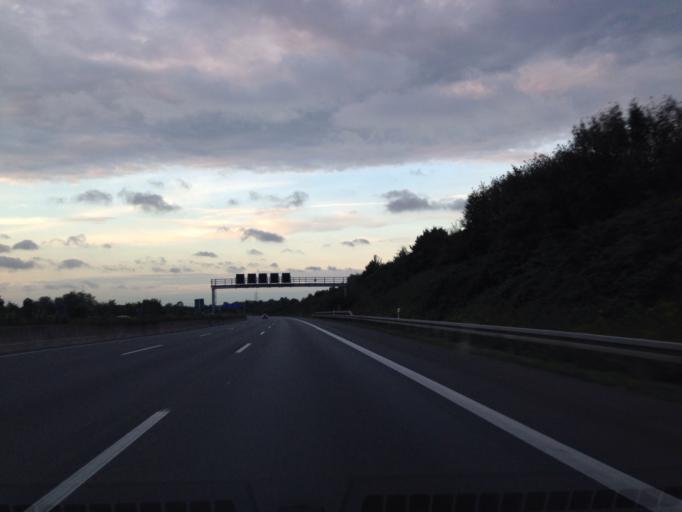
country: DE
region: North Rhine-Westphalia
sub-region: Regierungsbezirk Dusseldorf
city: Meerbusch
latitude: 51.2542
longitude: 6.6418
